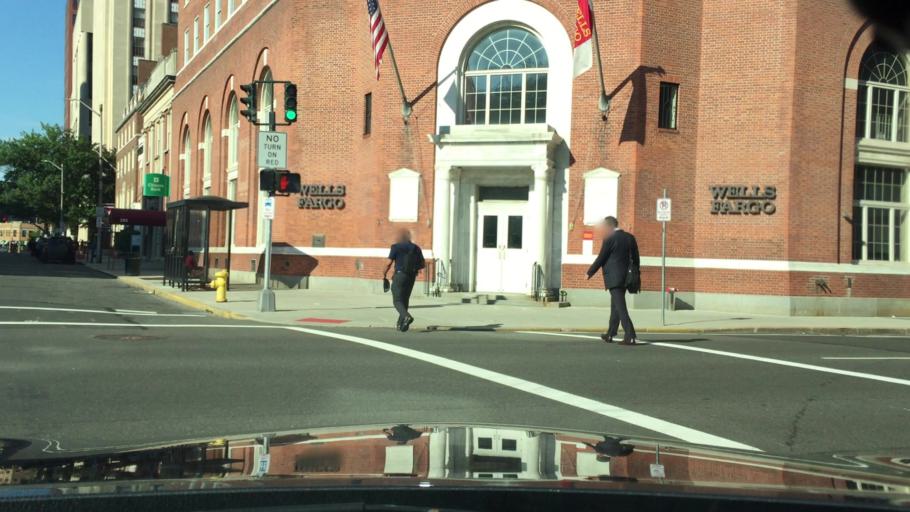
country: US
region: Connecticut
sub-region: New Haven County
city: New Haven
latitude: 41.3082
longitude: -72.9242
